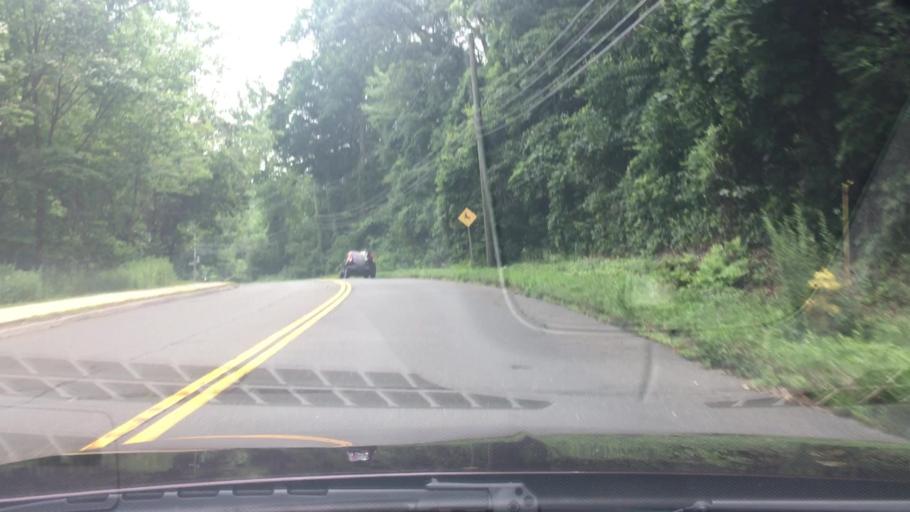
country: US
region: Connecticut
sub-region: Fairfield County
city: Danbury
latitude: 41.4309
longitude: -73.4248
